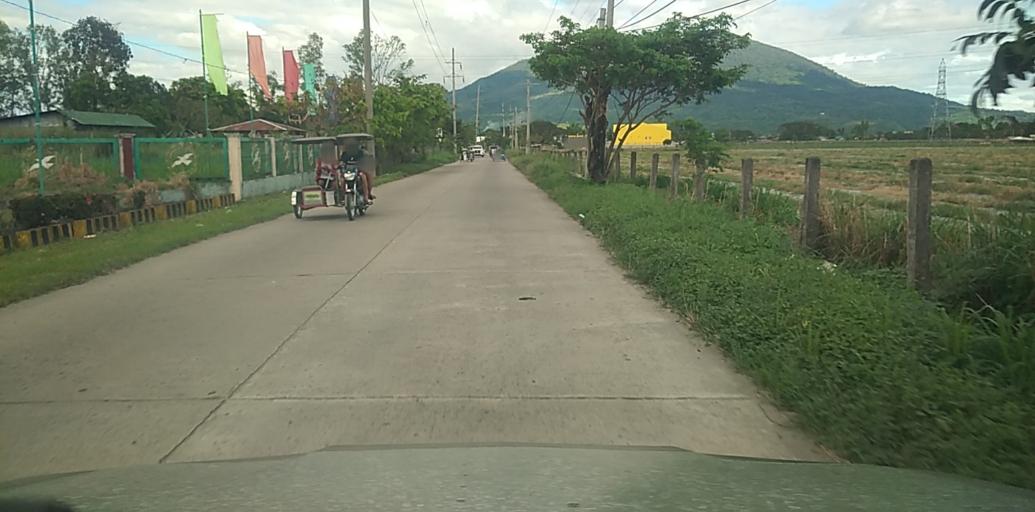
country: PH
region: Central Luzon
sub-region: Province of Pampanga
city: Arenas
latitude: 15.1745
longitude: 120.6756
